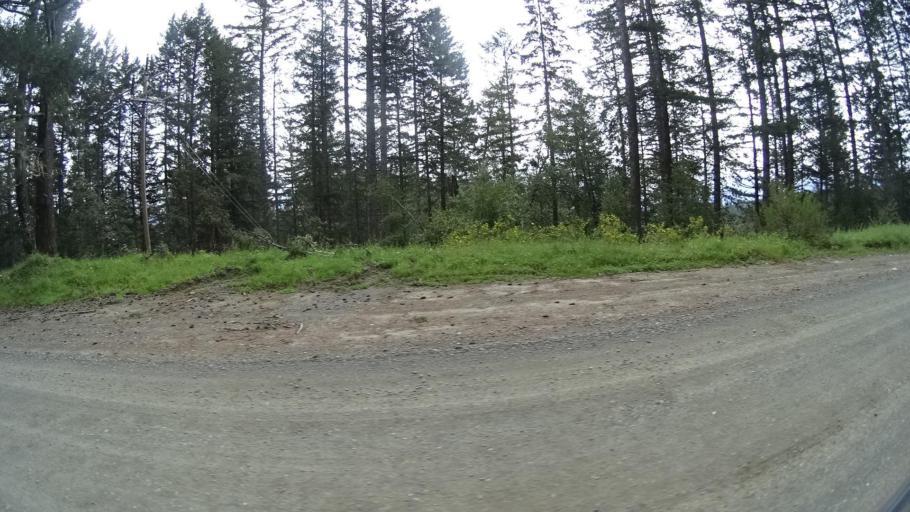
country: US
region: California
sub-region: Humboldt County
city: Redway
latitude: 40.2578
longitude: -123.7666
